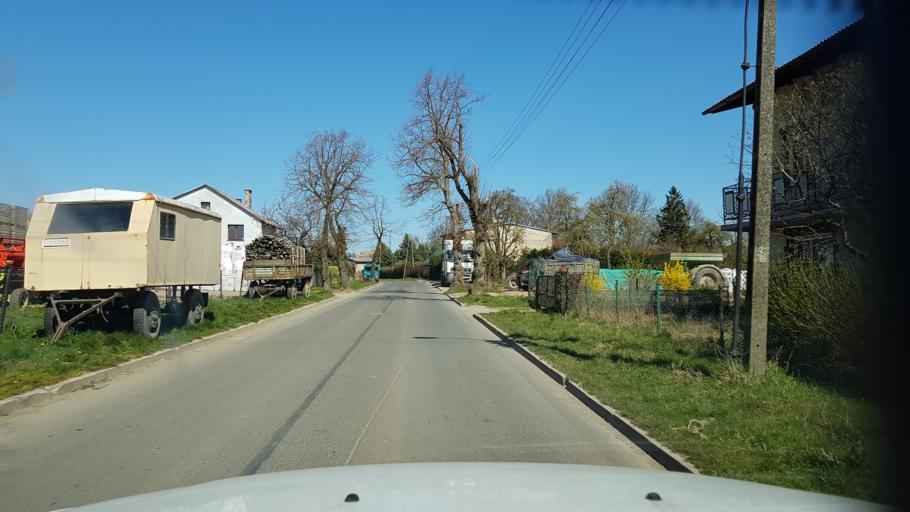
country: PL
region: West Pomeranian Voivodeship
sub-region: Koszalin
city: Koszalin
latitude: 54.2430
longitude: 16.1651
